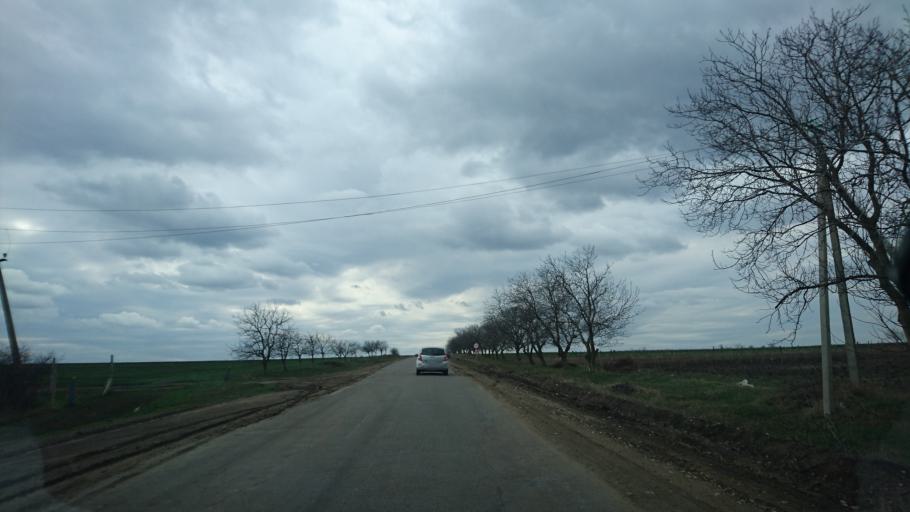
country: MD
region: Gagauzia
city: Comrat
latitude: 46.3079
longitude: 28.6112
